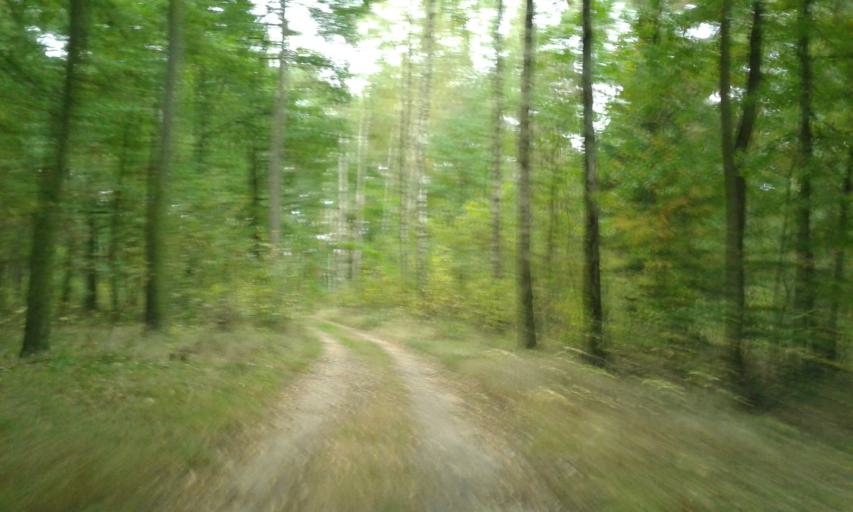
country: PL
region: West Pomeranian Voivodeship
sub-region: Powiat choszczenski
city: Pelczyce
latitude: 53.0685
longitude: 15.3006
